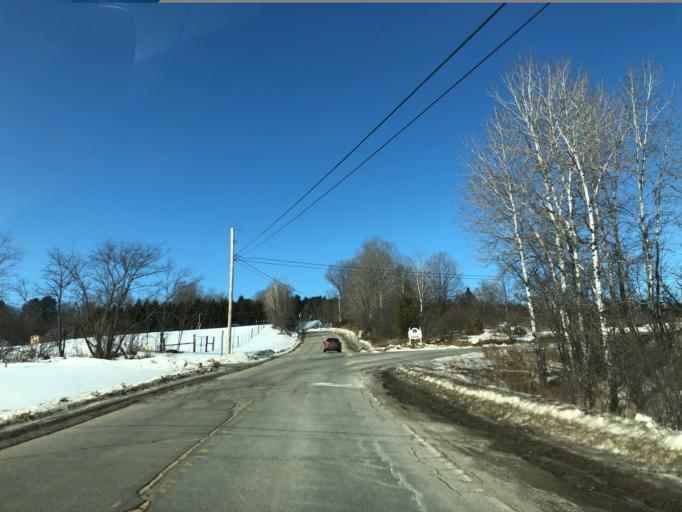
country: US
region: Maine
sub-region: Oxford County
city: Buckfield
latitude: 44.2593
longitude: -70.3379
